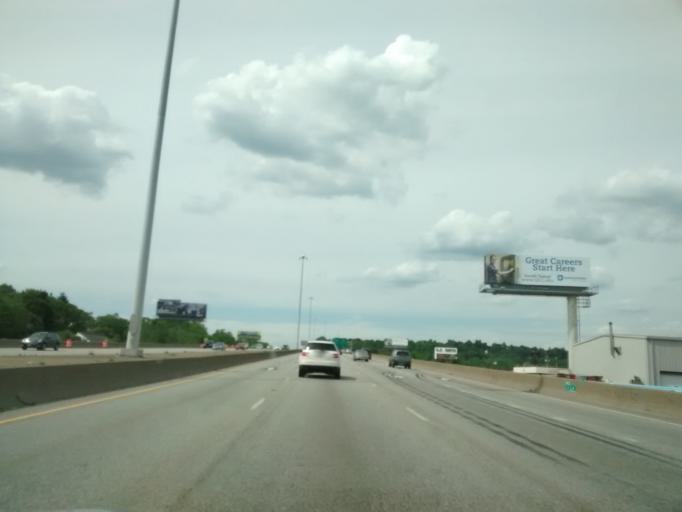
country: US
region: Massachusetts
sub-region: Worcester County
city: Worcester
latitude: 42.2809
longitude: -71.7977
